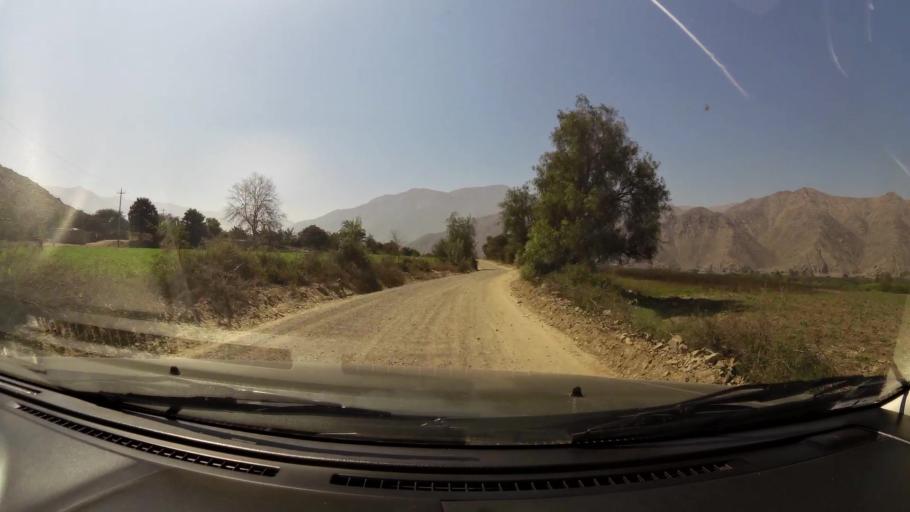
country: PE
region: Ica
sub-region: Provincia de Ica
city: Guadalupe
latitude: -13.8919
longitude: -75.6556
